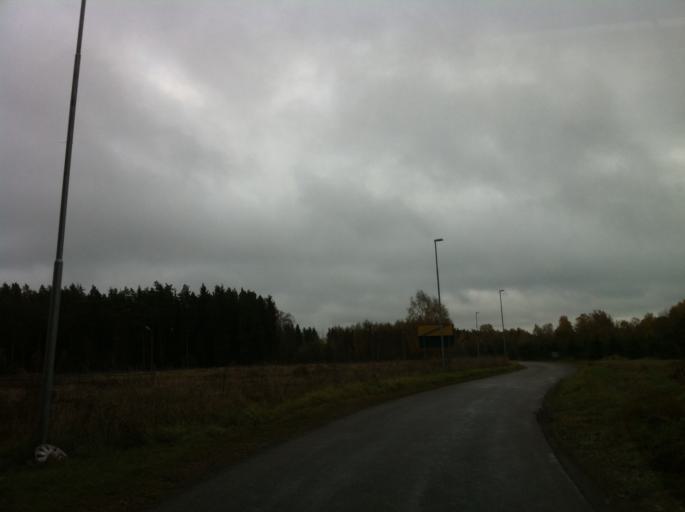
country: SE
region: Uppsala
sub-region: Osthammars Kommun
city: OEsthammar
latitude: 60.2662
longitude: 18.3435
